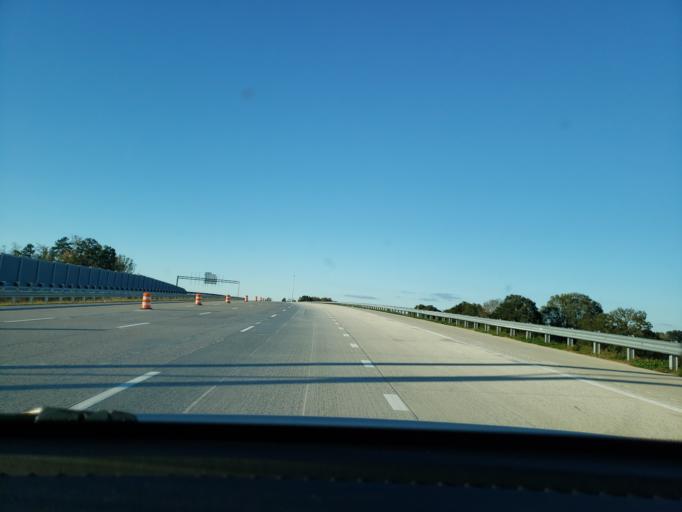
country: US
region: North Carolina
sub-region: Forsyth County
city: Walkertown
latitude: 36.1259
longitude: -80.1292
